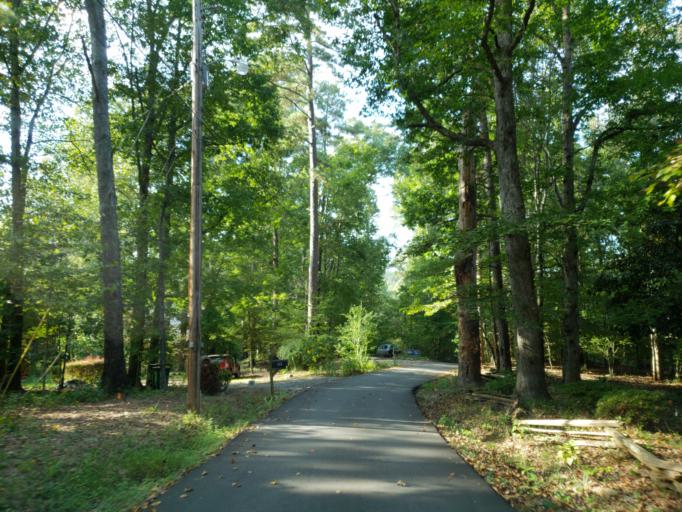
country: US
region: Georgia
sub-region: Fulton County
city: Roswell
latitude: 34.0829
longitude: -84.4085
